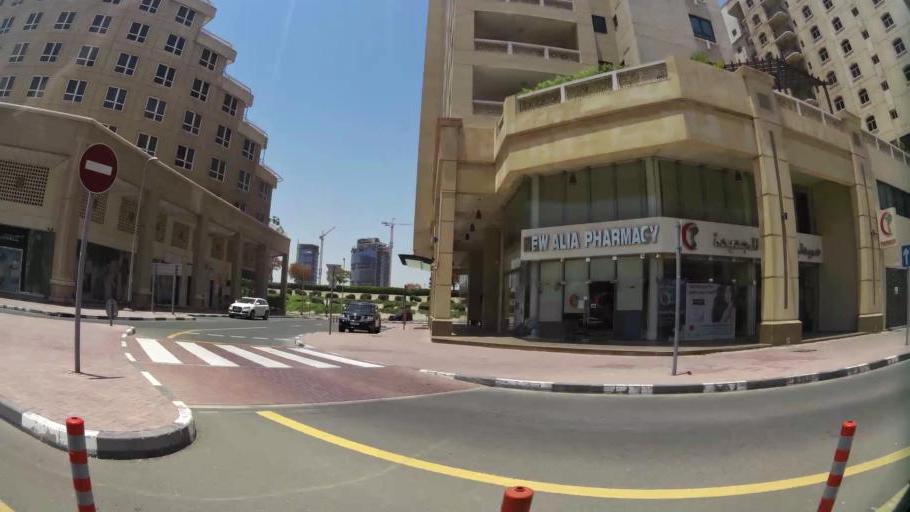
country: AE
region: Ash Shariqah
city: Sharjah
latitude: 25.2559
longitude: 55.3267
